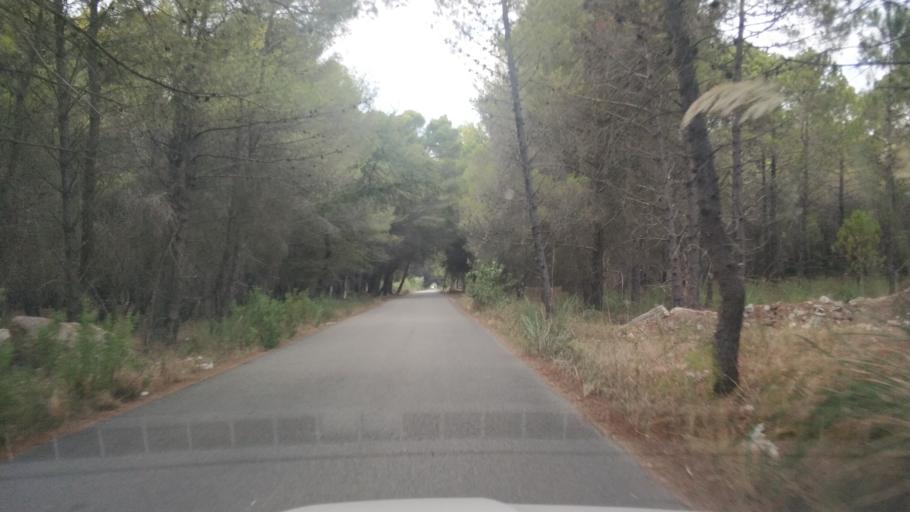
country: AL
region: Vlore
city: Vlore
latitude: 40.4949
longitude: 19.4338
